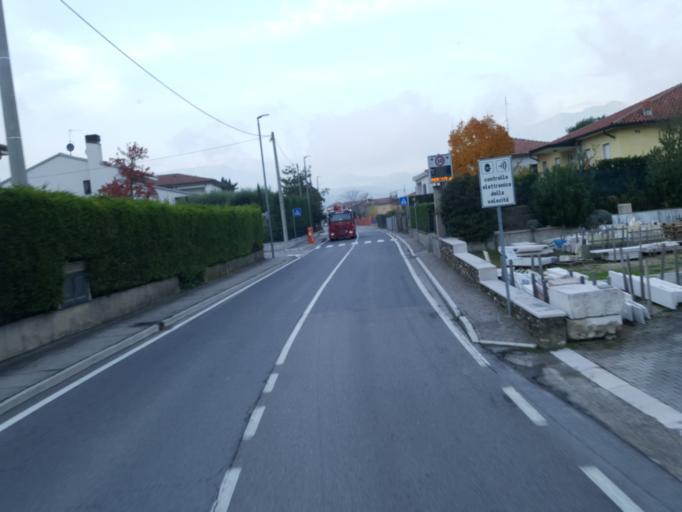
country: IT
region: Veneto
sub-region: Provincia di Verona
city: Pastrengo
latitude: 45.5187
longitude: 10.8018
